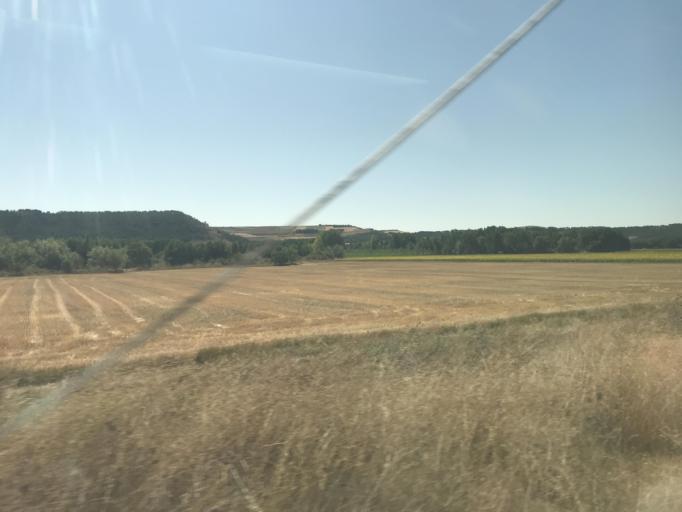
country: ES
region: Castille and Leon
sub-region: Provincia de Burgos
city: Villaldemiro
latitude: 42.2338
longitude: -3.9798
